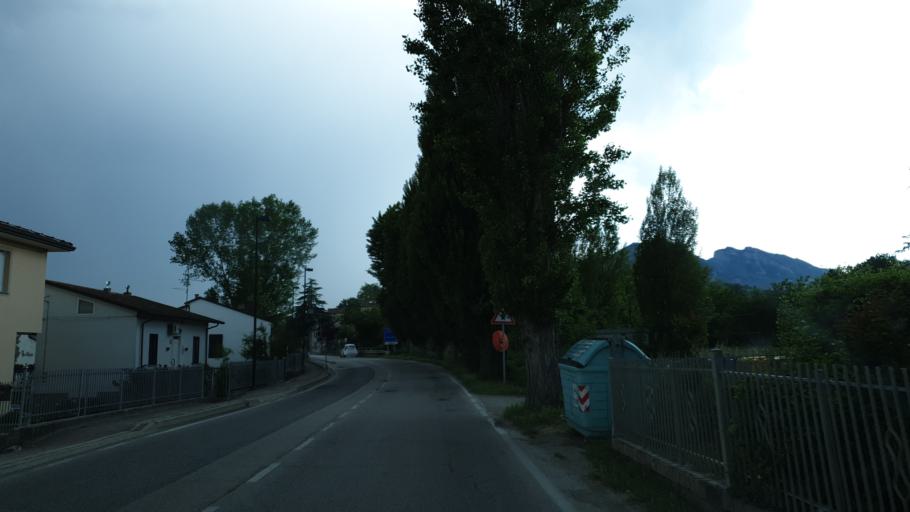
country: IT
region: Emilia-Romagna
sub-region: Provincia di Rimini
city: Secchiano
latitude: 43.9221
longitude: 12.3137
